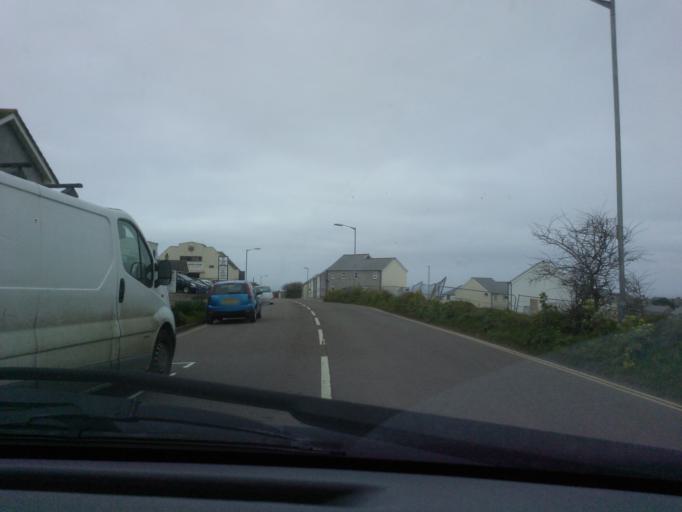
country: GB
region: England
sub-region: Cornwall
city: Saint Just
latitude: 50.1216
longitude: -5.6765
